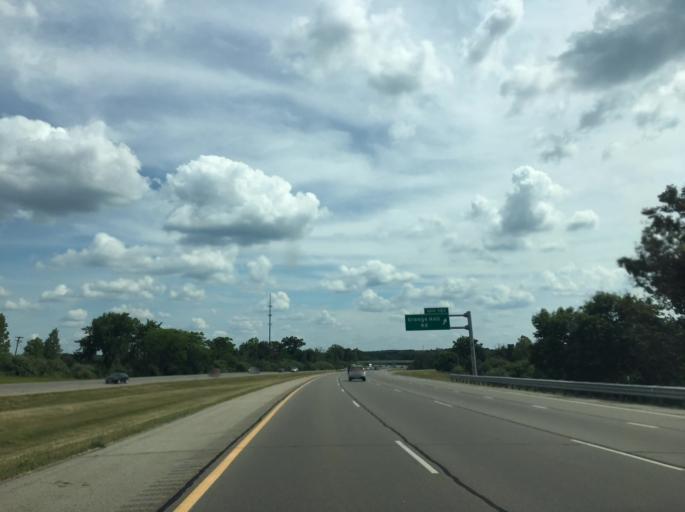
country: US
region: Michigan
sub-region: Oakland County
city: Holly
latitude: 42.8213
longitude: -83.5706
